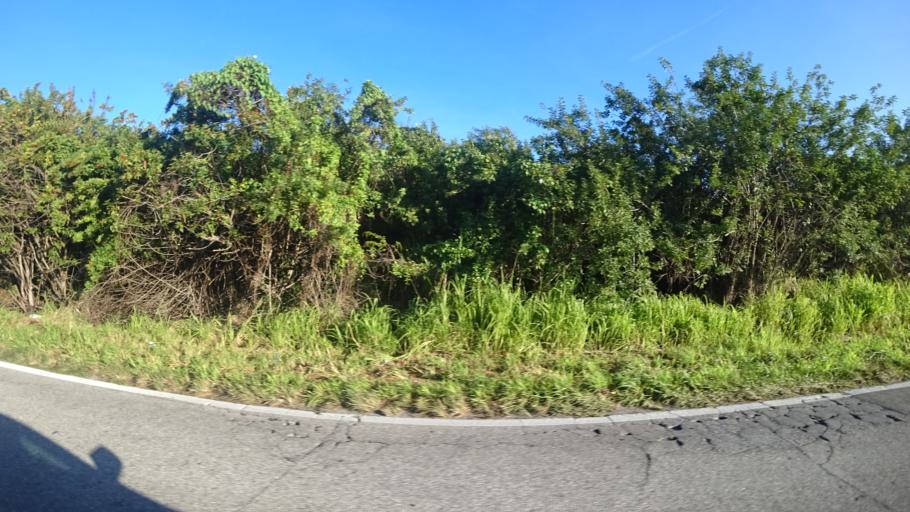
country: US
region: Florida
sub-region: Manatee County
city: Memphis
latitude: 27.5579
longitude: -82.5513
